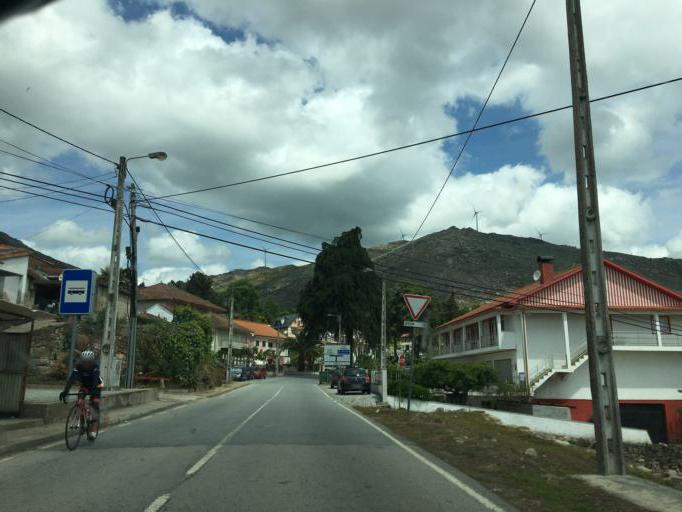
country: PT
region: Vila Real
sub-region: Boticas
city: Boticas
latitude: 41.7094
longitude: -7.6409
